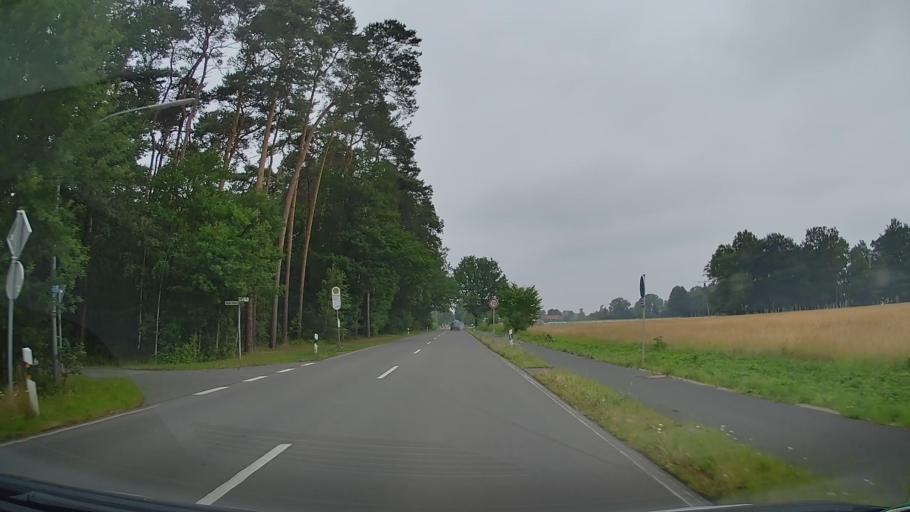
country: DE
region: North Rhine-Westphalia
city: Espelkamp
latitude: 52.3989
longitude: 8.6229
